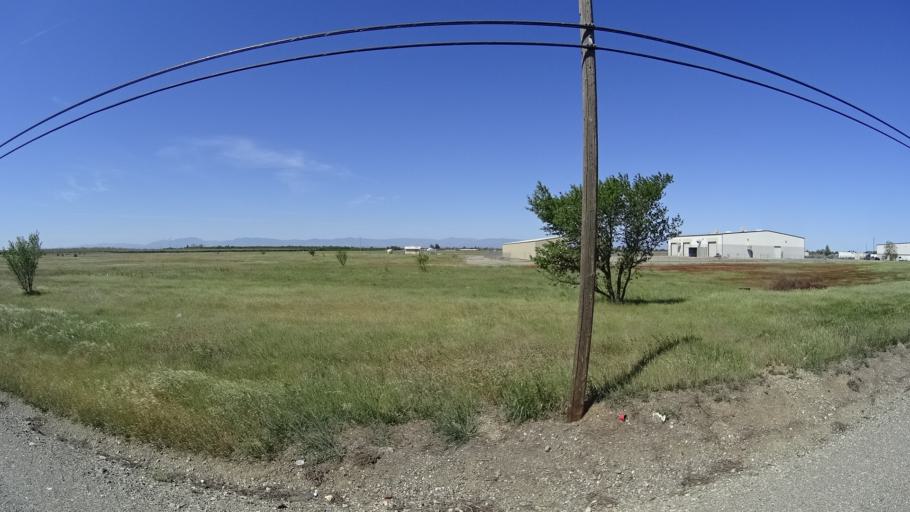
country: US
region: California
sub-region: Glenn County
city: Orland
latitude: 39.7164
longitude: -122.1411
